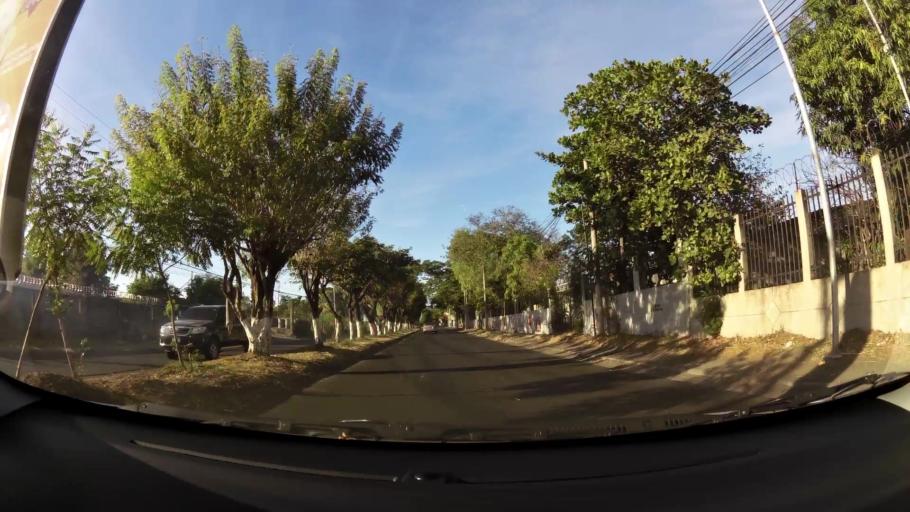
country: SV
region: San Miguel
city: San Miguel
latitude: 13.4541
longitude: -88.1591
